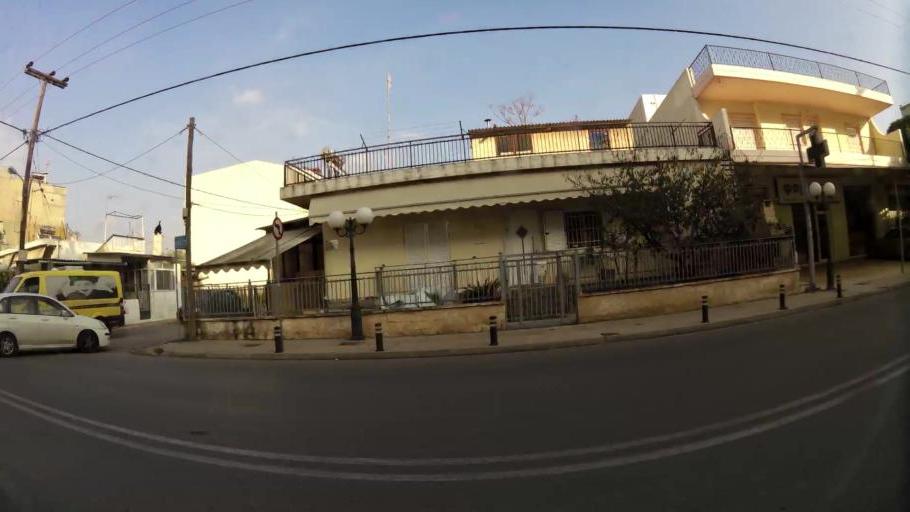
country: GR
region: Attica
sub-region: Nomarchia Anatolikis Attikis
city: Acharnes
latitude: 38.0853
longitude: 23.7453
